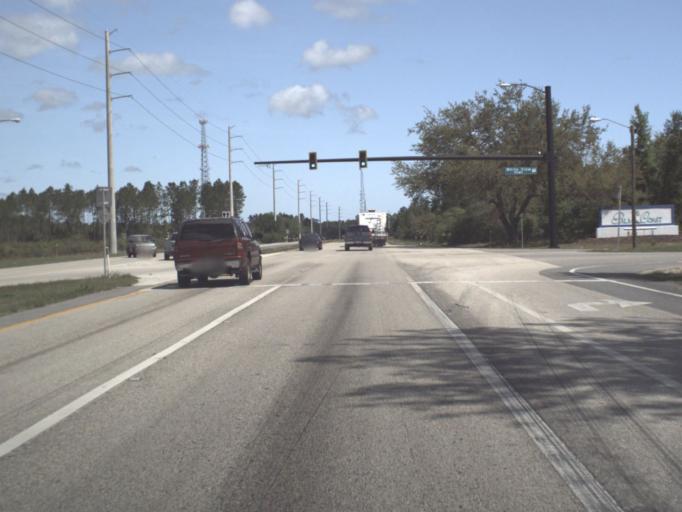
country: US
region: Florida
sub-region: Flagler County
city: Bunnell
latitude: 29.5222
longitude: -81.2627
